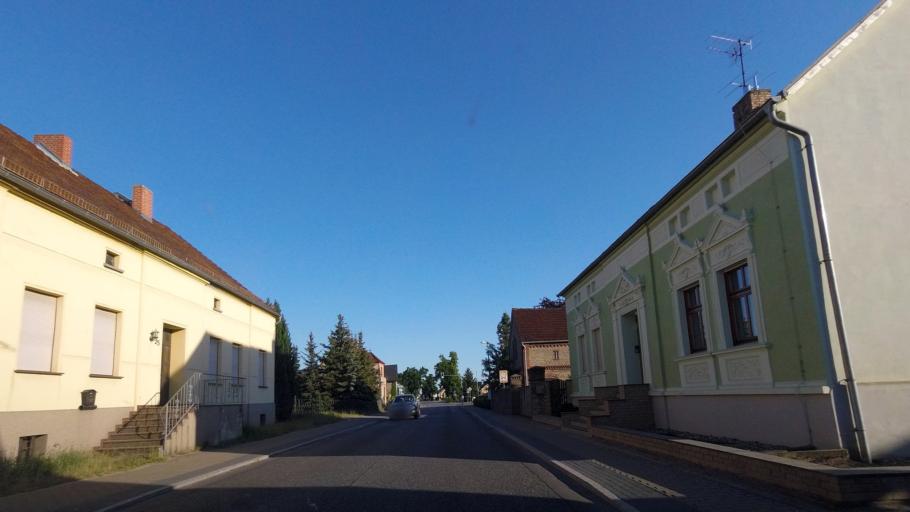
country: DE
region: Brandenburg
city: Golzow
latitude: 52.2851
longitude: 12.6021
